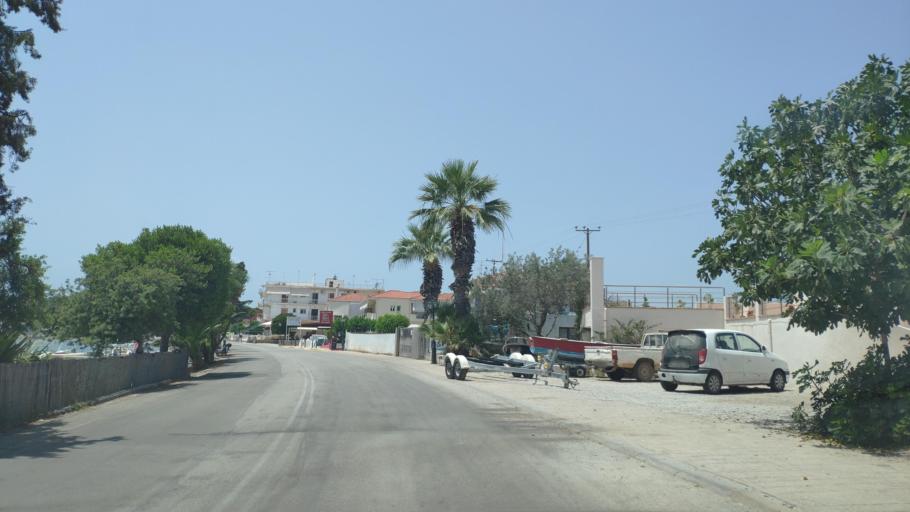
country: GR
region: Peloponnese
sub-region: Nomos Argolidos
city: Porto Cheli
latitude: 37.3276
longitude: 23.1500
